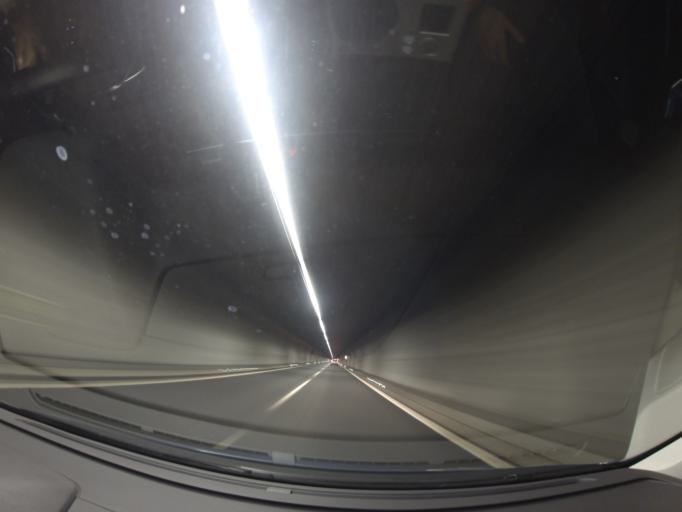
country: CH
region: Saint Gallen
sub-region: Wahlkreis See-Gaster
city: Amden
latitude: 47.1177
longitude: 9.1664
